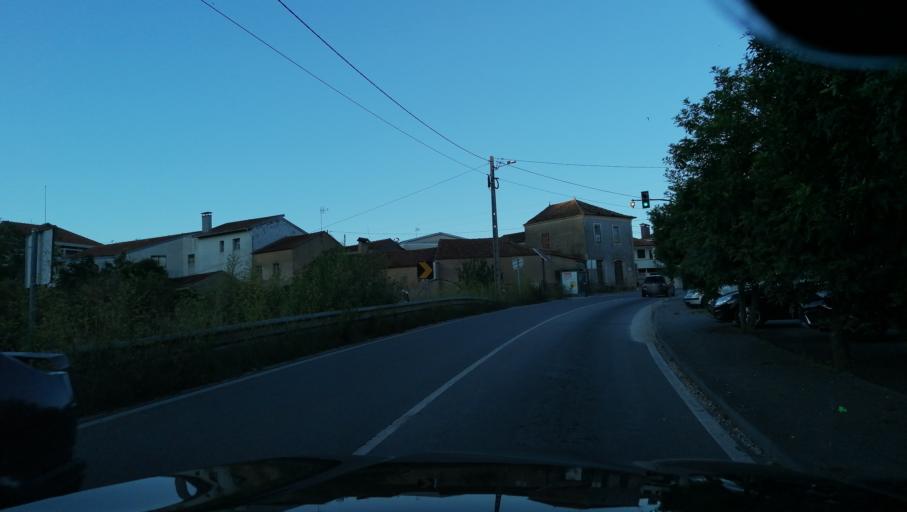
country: PT
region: Aveiro
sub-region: Oliveira do Bairro
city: Oliveira do Bairro
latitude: 40.5570
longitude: -8.4898
